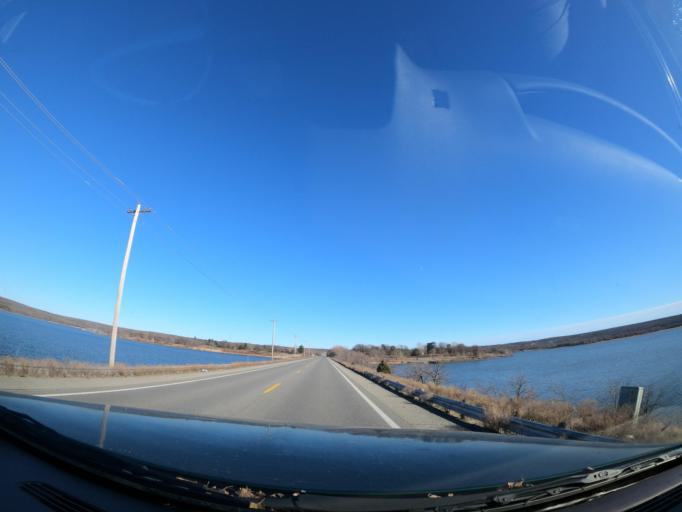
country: US
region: Oklahoma
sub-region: Pittsburg County
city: Longtown
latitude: 35.2392
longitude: -95.4999
